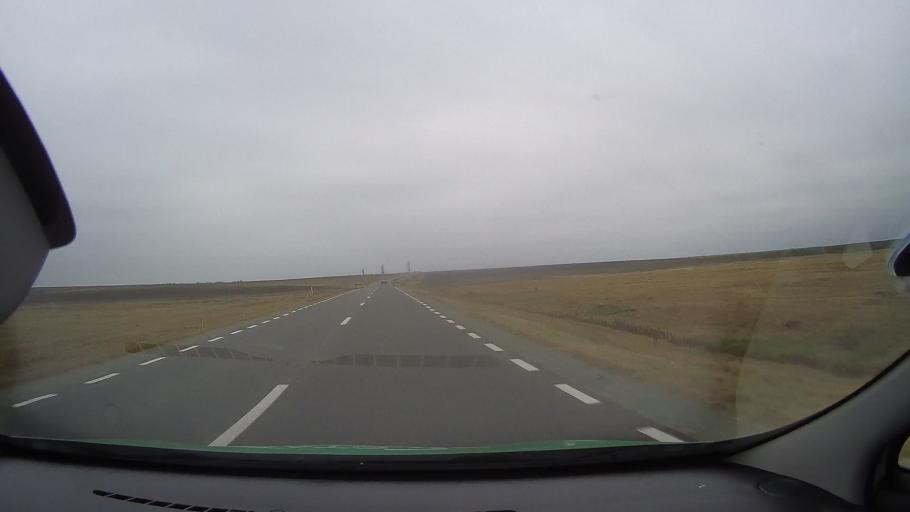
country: RO
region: Ialomita
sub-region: Comuna Scanteia
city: Iazu
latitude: 44.7219
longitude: 27.4221
